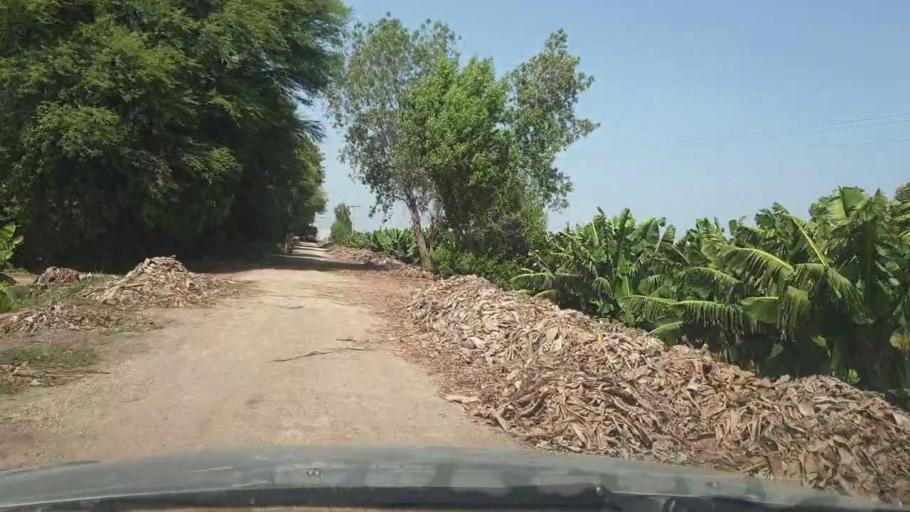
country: PK
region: Sindh
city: Tando Ghulam Ali
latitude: 25.1485
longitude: 68.8860
